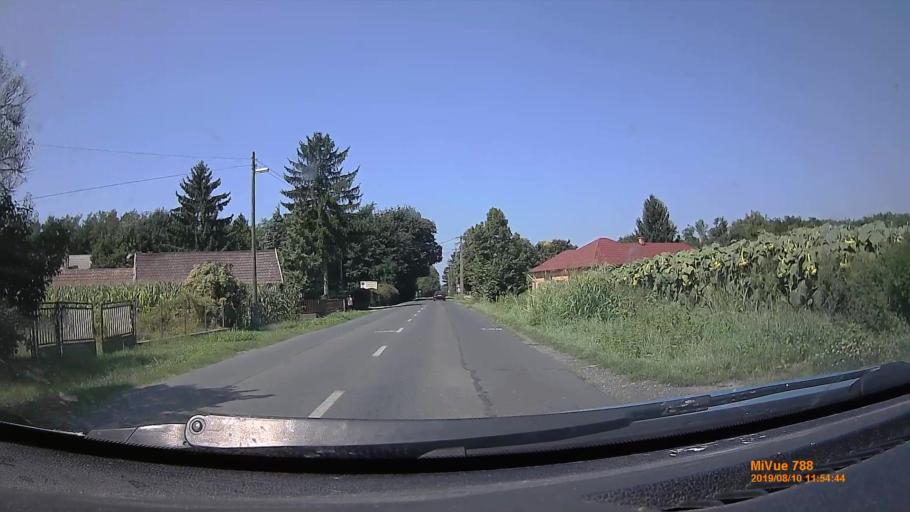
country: HU
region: Somogy
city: Somogyvar
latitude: 46.5203
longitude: 17.6840
